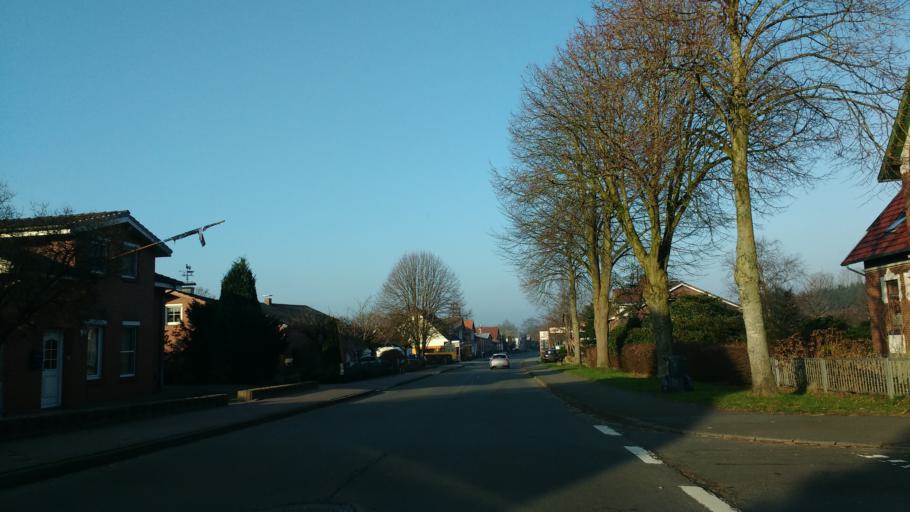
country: DE
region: Schleswig-Holstein
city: Wacken
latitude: 54.0222
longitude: 9.3721
